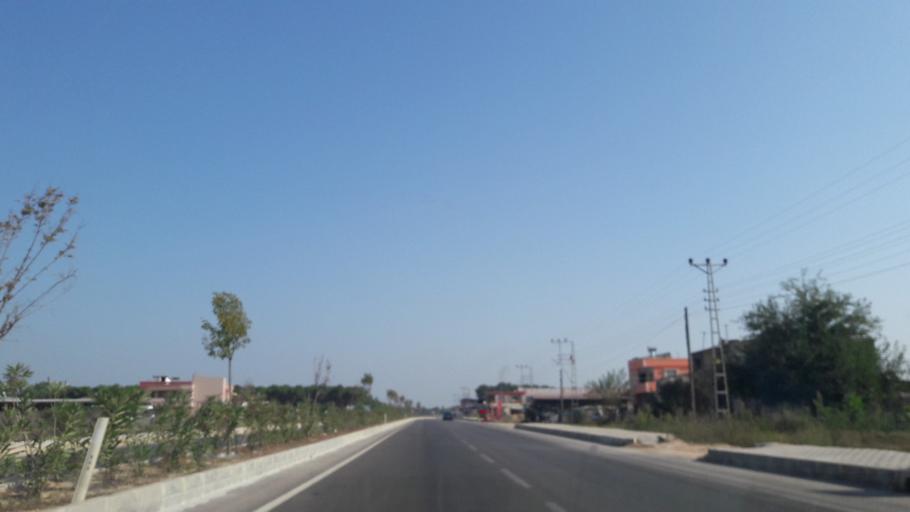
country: TR
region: Adana
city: Yakapinar
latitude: 37.1153
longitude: 35.5132
